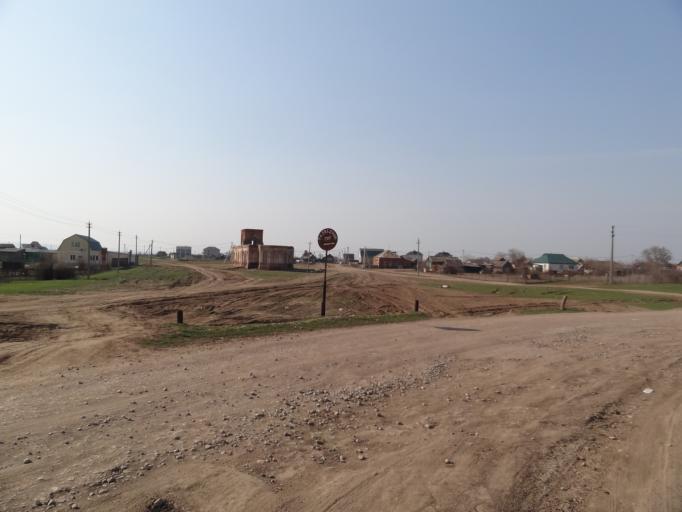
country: RU
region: Saratov
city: Privolzhskiy
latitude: 51.3241
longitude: 45.9783
